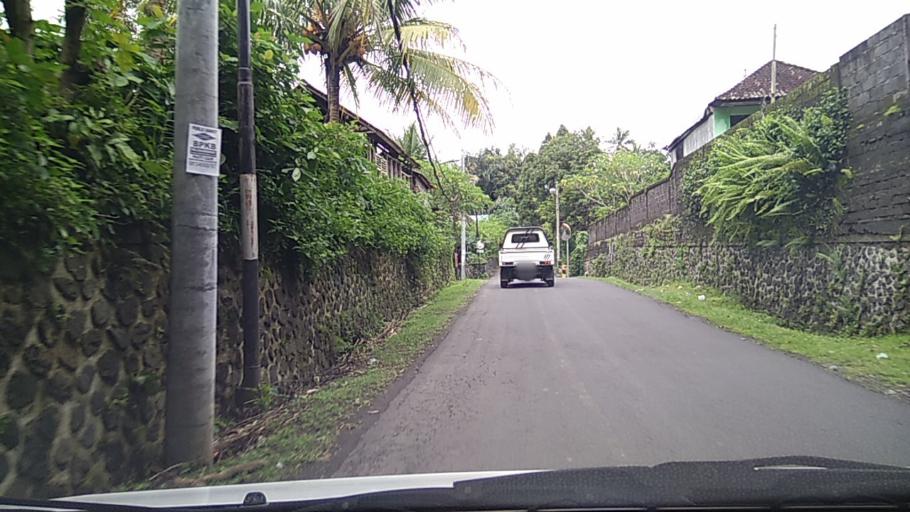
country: ID
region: Bali
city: Banjar Sempidi
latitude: -8.5220
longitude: 115.2137
